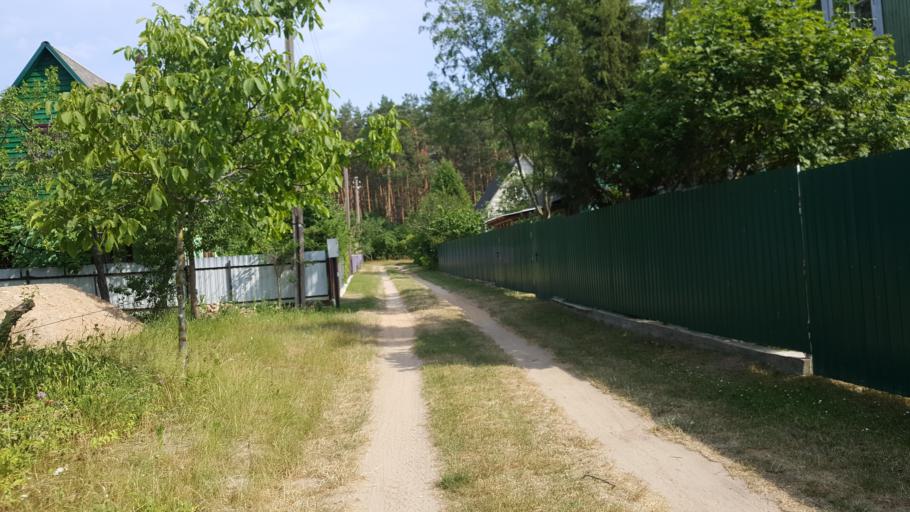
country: BY
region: Brest
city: Kamyanyets
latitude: 52.3666
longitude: 23.8073
